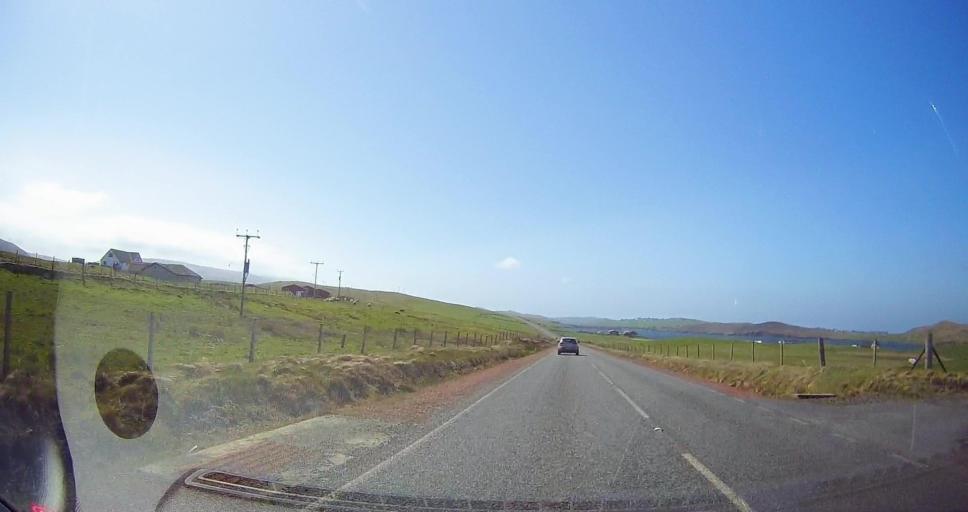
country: GB
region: Scotland
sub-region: Shetland Islands
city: Sandwick
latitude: 60.1208
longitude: -1.2884
